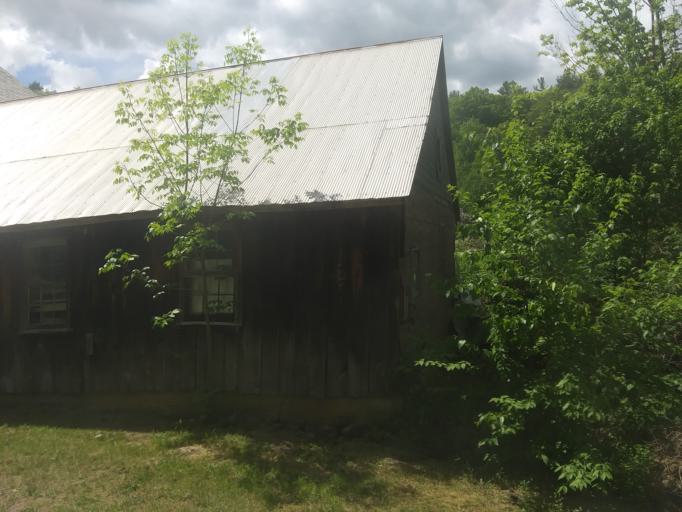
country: US
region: Massachusetts
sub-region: Franklin County
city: Buckland
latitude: 42.5740
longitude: -72.7732
